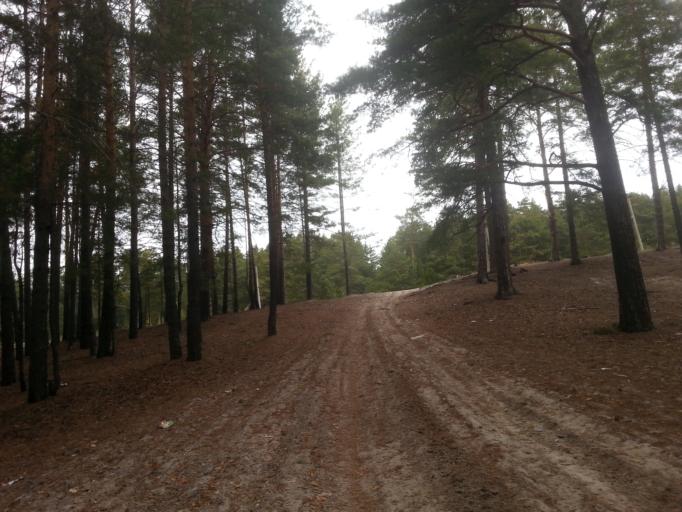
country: RU
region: Altai Krai
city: Yuzhnyy
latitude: 53.3139
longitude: 83.6901
